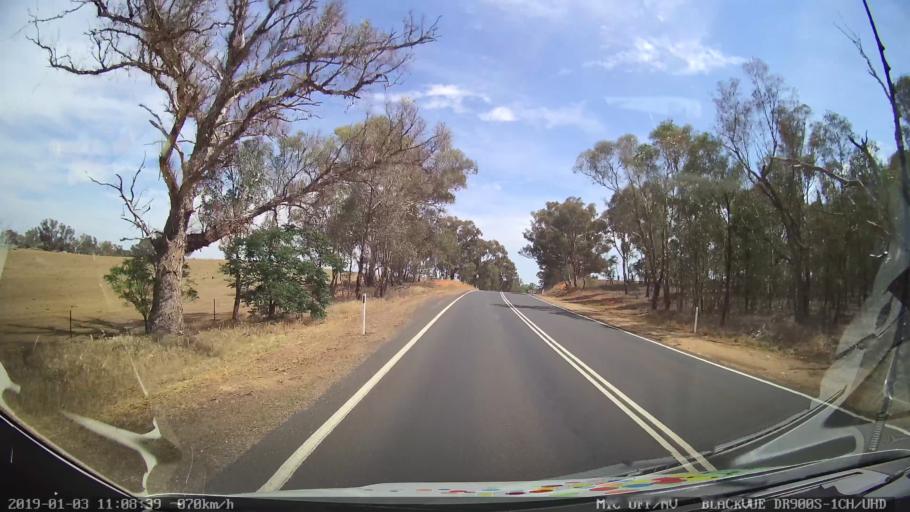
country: AU
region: New South Wales
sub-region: Young
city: Young
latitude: -34.2471
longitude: 148.2562
